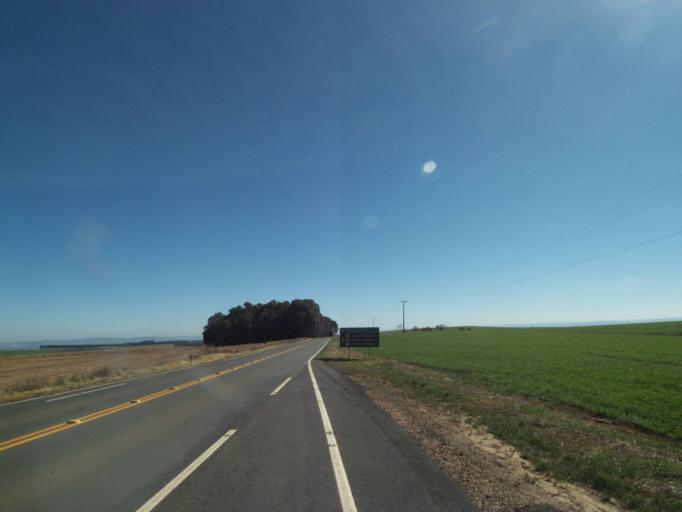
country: BR
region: Parana
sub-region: Tibagi
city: Tibagi
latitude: -24.5825
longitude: -50.2676
